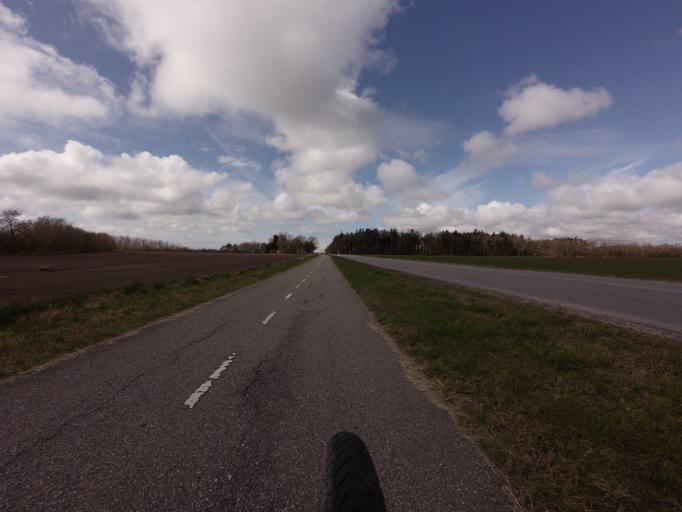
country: DK
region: North Denmark
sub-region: Hjorring Kommune
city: Vra
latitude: 57.3559
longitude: 9.8879
